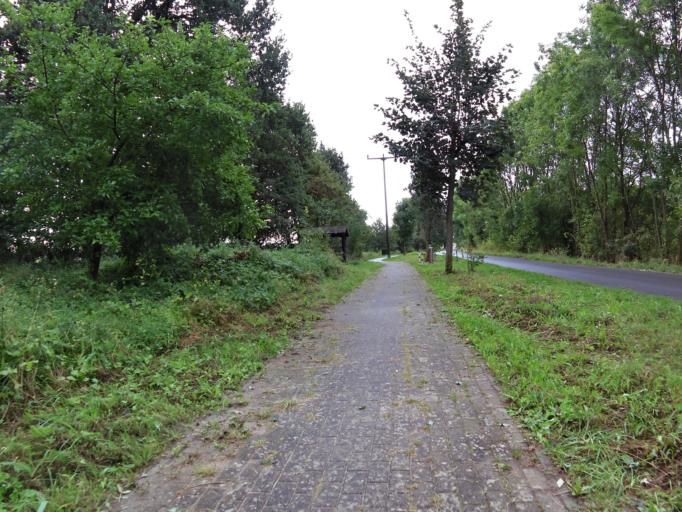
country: DE
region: Saxony-Anhalt
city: Sandau
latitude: 52.7543
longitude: 12.0189
